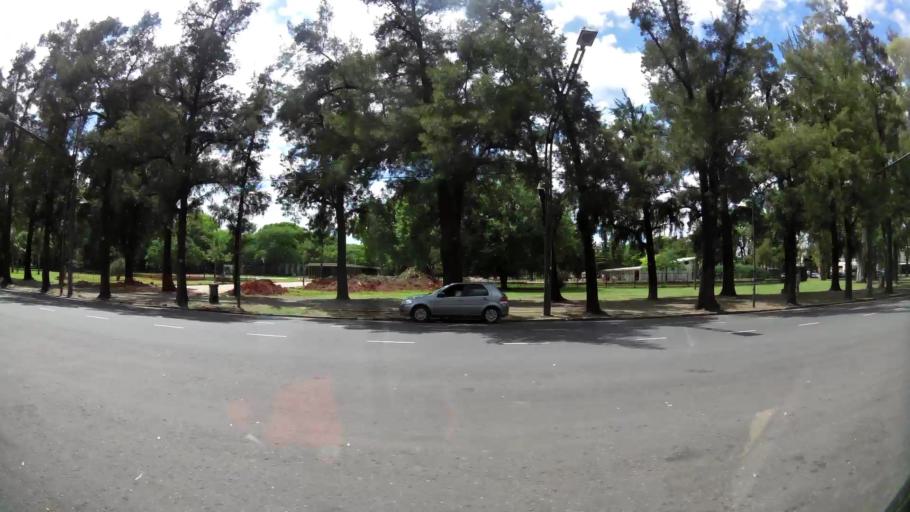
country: AR
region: Santa Fe
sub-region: Departamento de Rosario
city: Rosario
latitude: -32.9642
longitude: -60.6585
